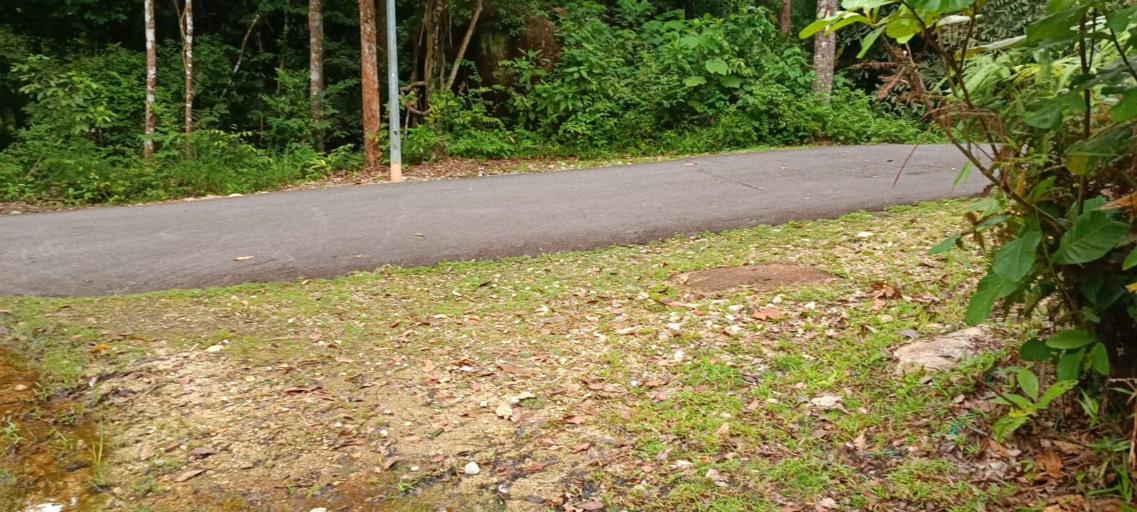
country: MY
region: Penang
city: Kampung Sungai Ara
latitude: 5.3974
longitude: 100.2608
